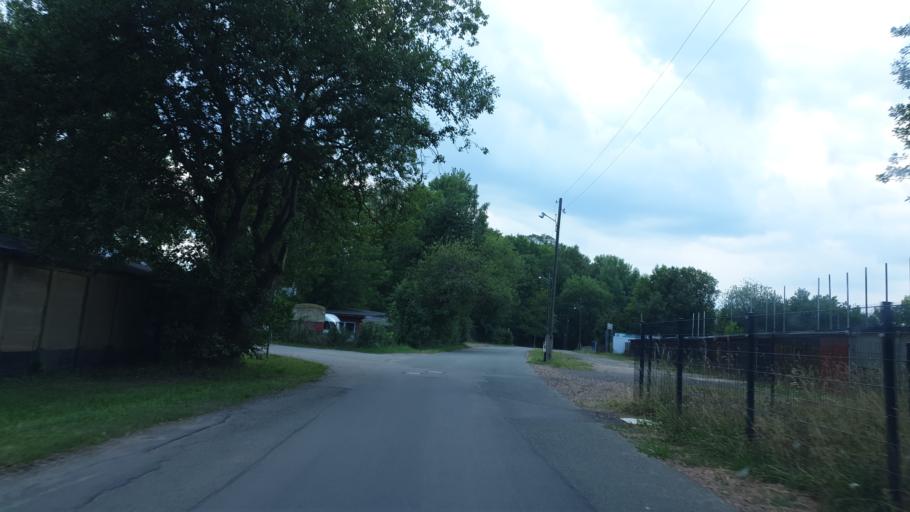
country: DE
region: Saxony
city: Lugau
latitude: 50.7351
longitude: 12.7335
